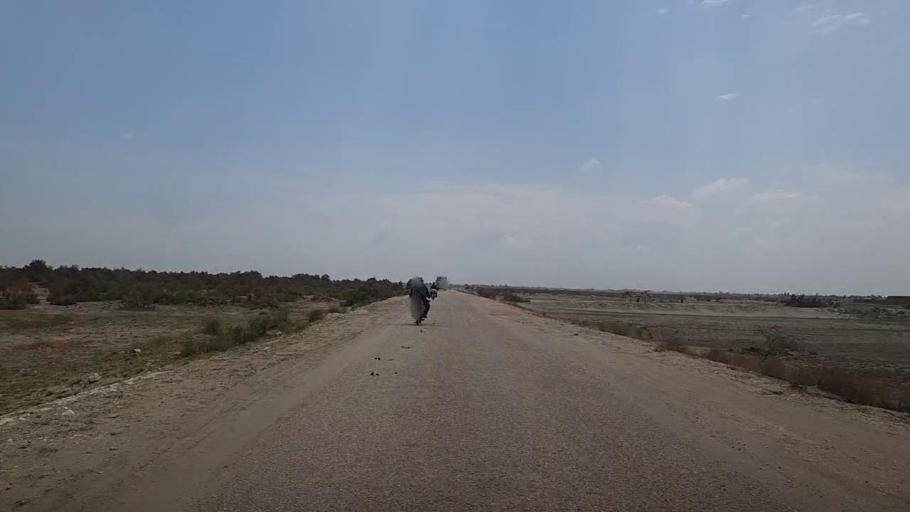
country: PK
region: Sindh
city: Kandhkot
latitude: 28.2887
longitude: 69.1485
